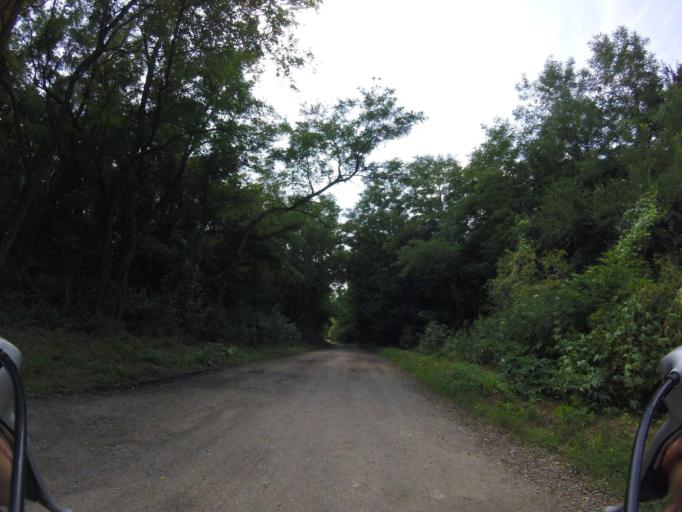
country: SK
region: Nitriansky
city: Sahy
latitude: 48.0444
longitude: 18.8485
